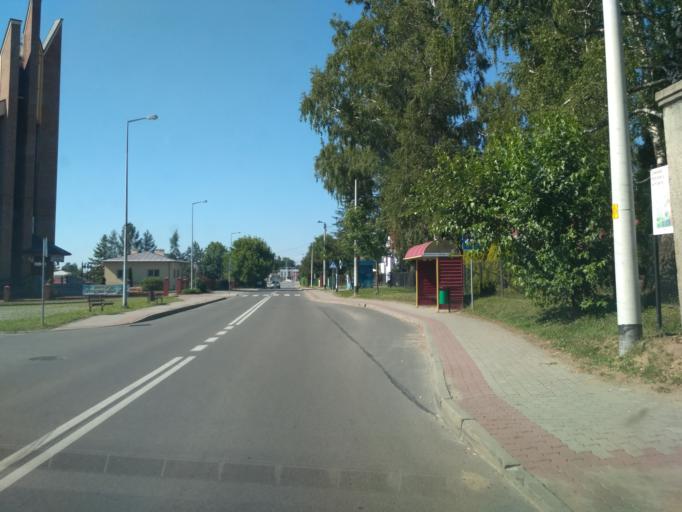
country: PL
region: Subcarpathian Voivodeship
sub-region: Krosno
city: Krosno
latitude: 49.6798
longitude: 21.7672
